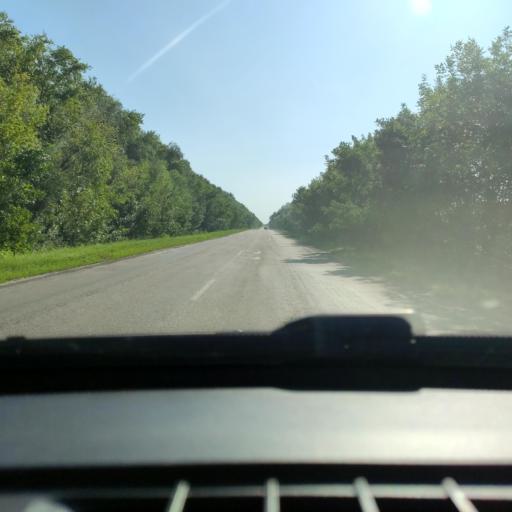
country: RU
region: Voronezj
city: Panino
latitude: 51.5813
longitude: 39.9455
